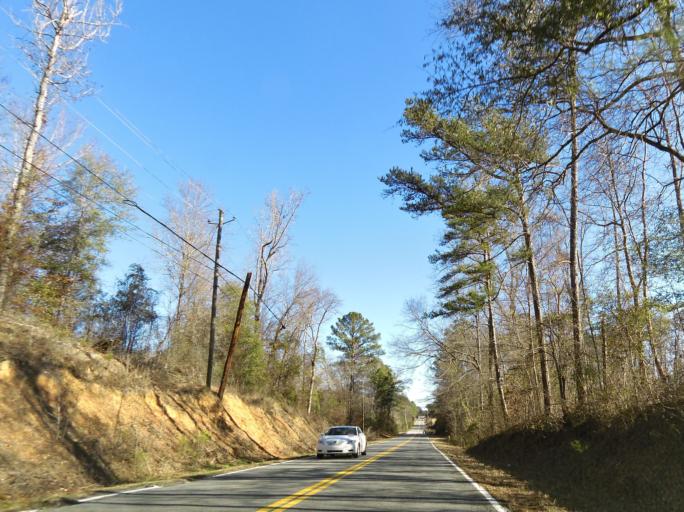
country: US
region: Georgia
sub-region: Bibb County
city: West Point
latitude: 32.7956
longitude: -83.7566
